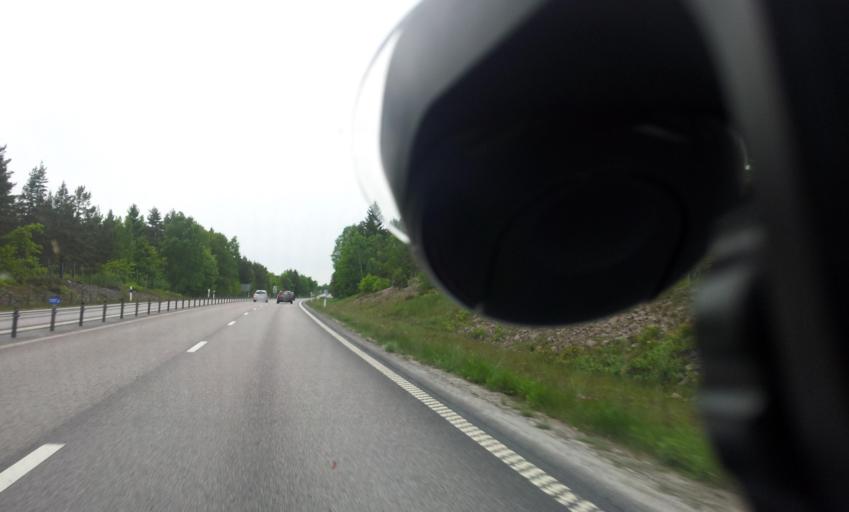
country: SE
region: Kalmar
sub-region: Oskarshamns Kommun
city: Paskallavik
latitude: 57.1355
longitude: 16.4726
